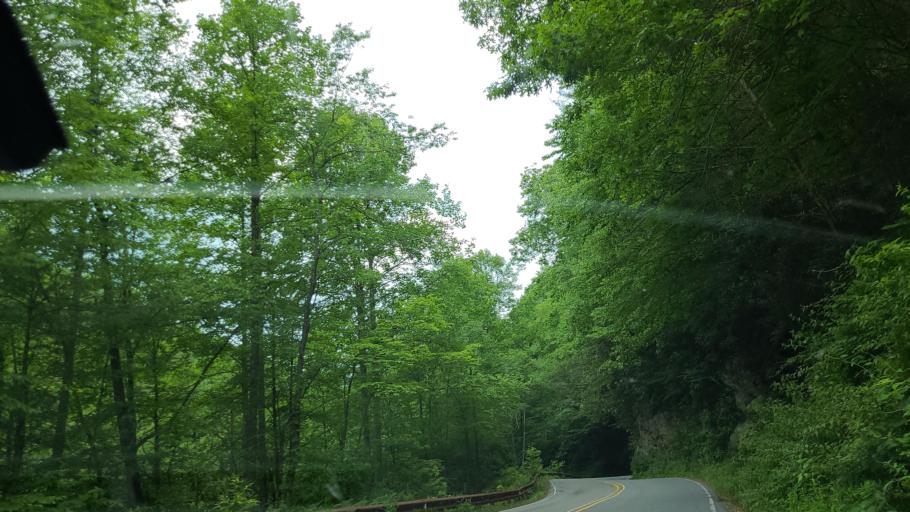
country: US
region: North Carolina
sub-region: Macon County
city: Franklin
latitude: 35.0819
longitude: -83.2633
